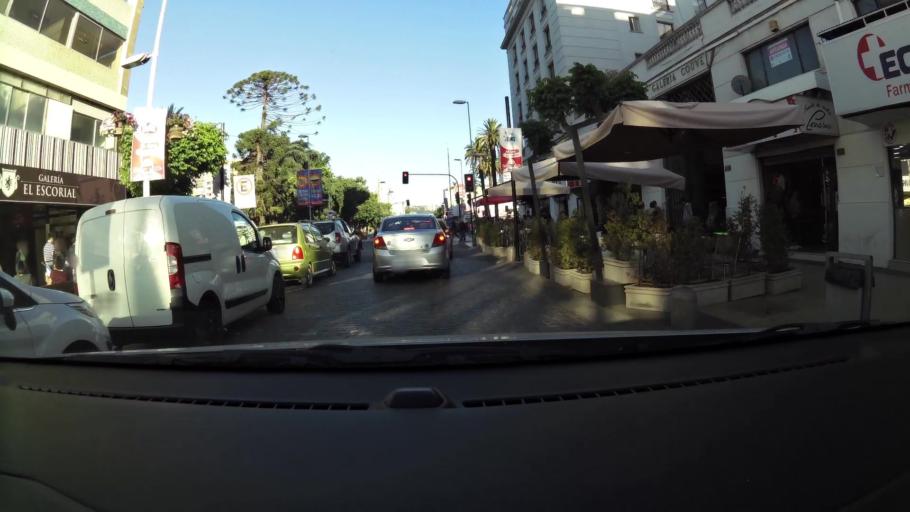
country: CL
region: Valparaiso
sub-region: Provincia de Valparaiso
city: Vina del Mar
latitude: -33.0249
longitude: -71.5528
